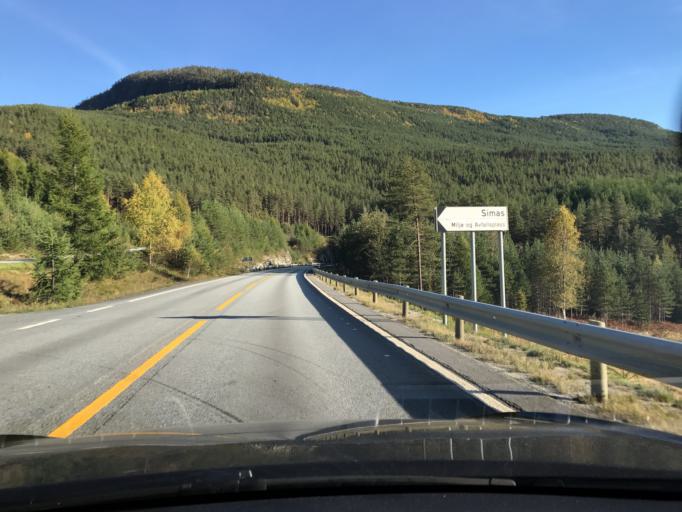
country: NO
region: Sogn og Fjordane
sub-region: Laerdal
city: Laerdalsoyri
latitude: 61.1812
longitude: 7.2957
